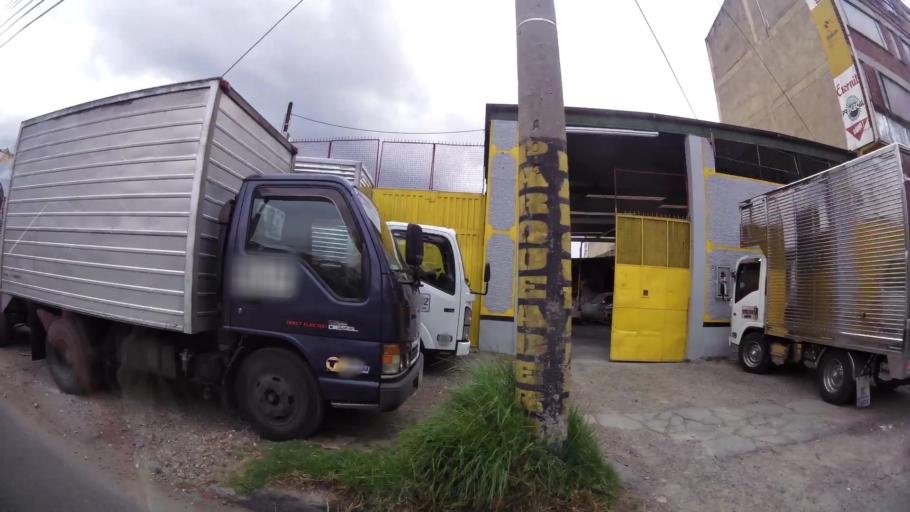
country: CO
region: Bogota D.C.
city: Bogota
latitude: 4.6086
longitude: -74.1018
